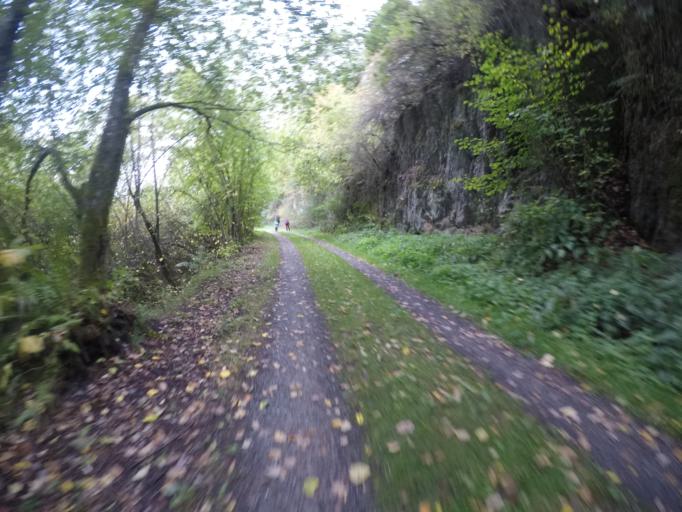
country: BE
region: Wallonia
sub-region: Province du Luxembourg
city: Fauvillers
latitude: 49.8827
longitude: 5.6729
